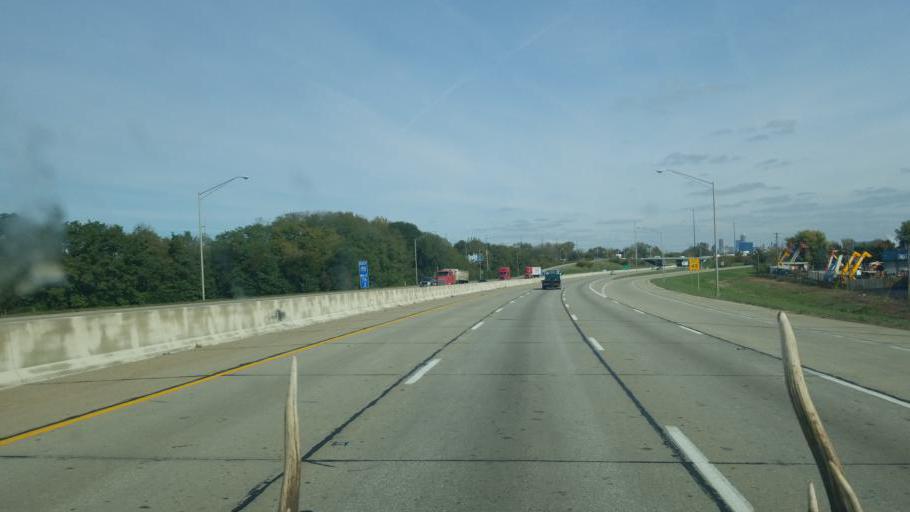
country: US
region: Indiana
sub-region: Marion County
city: Speedway
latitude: 39.7502
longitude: -86.2318
